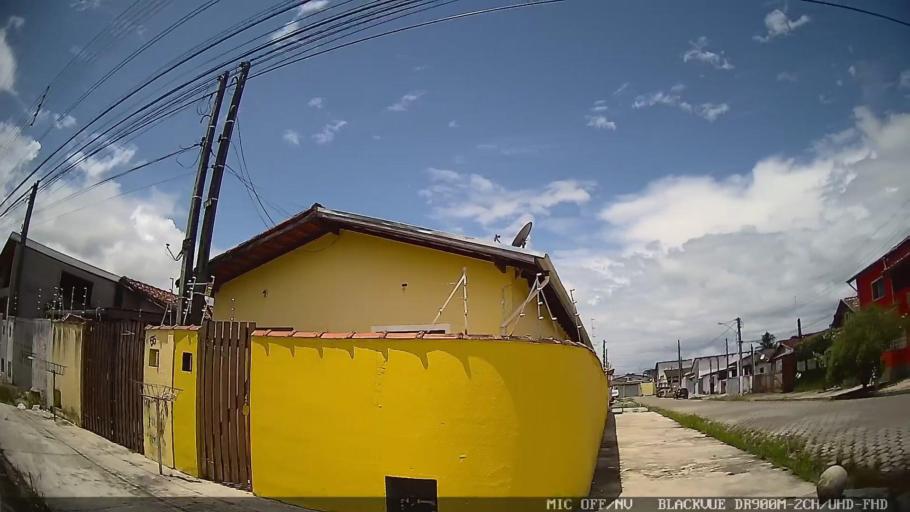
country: BR
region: Sao Paulo
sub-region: Caraguatatuba
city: Caraguatatuba
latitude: -23.6403
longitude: -45.4329
